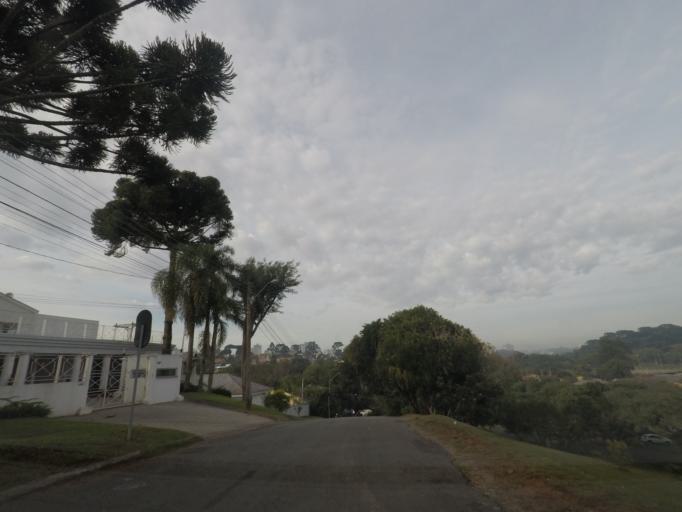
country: BR
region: Parana
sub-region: Curitiba
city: Curitiba
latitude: -25.4205
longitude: -49.3050
